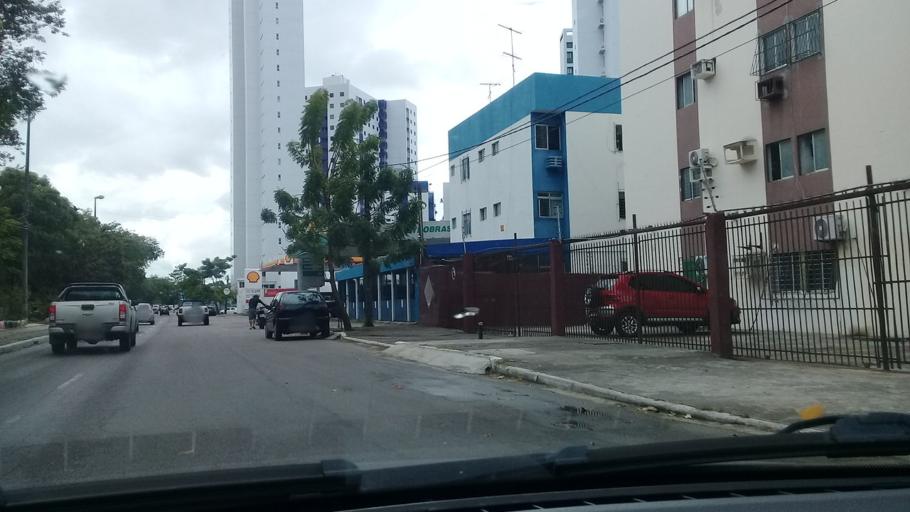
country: BR
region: Pernambuco
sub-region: Recife
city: Recife
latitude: -8.1349
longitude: -34.9090
